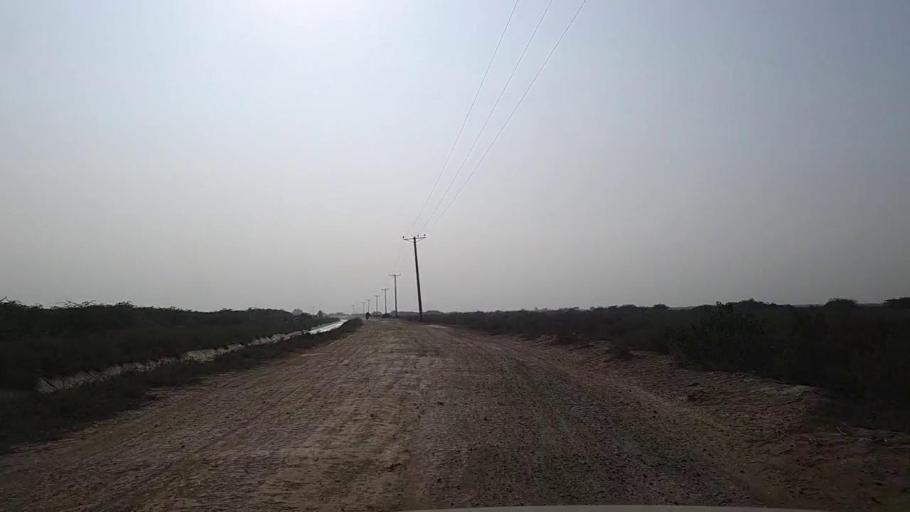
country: PK
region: Sindh
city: Keti Bandar
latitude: 24.1957
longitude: 67.6149
